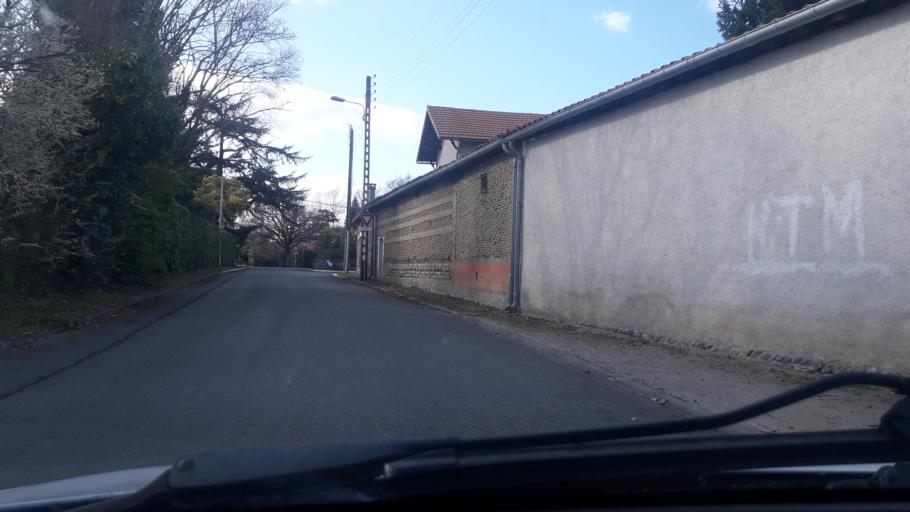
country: FR
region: Midi-Pyrenees
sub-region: Departement de la Haute-Garonne
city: Carbonne
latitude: 43.2959
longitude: 1.2137
